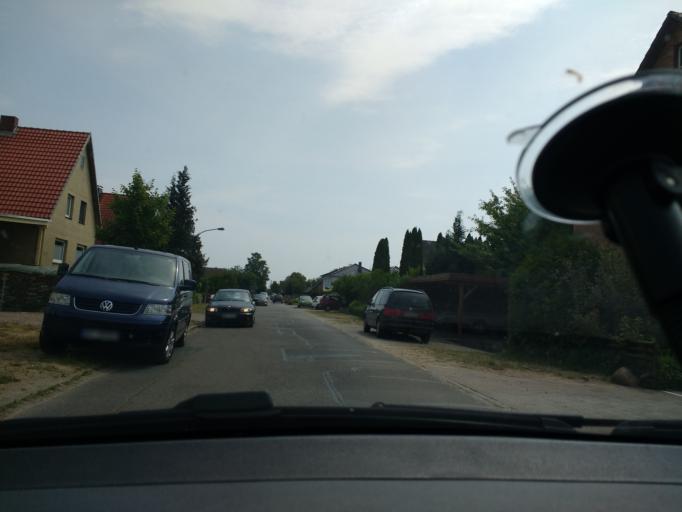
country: DE
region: Lower Saxony
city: Sassenburg
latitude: 52.5248
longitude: 10.5893
